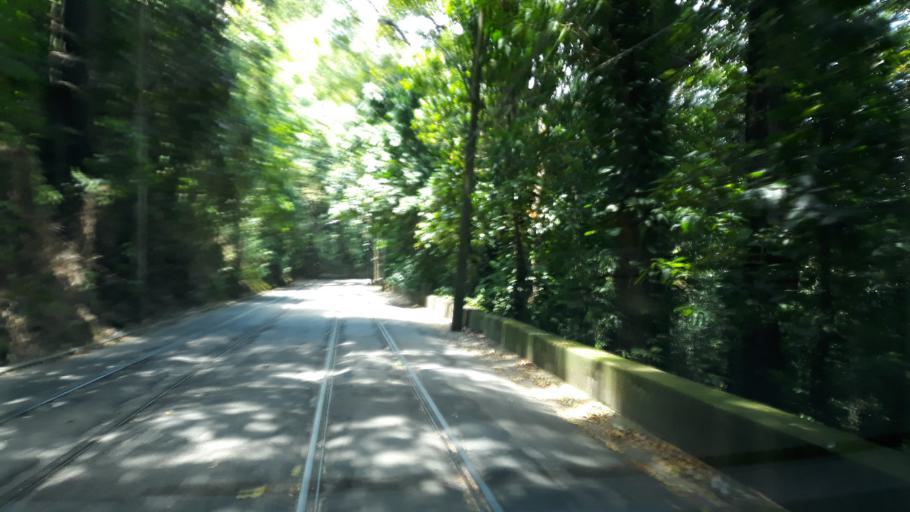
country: BR
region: Rio de Janeiro
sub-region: Rio De Janeiro
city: Rio de Janeiro
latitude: -22.9404
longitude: -43.2102
